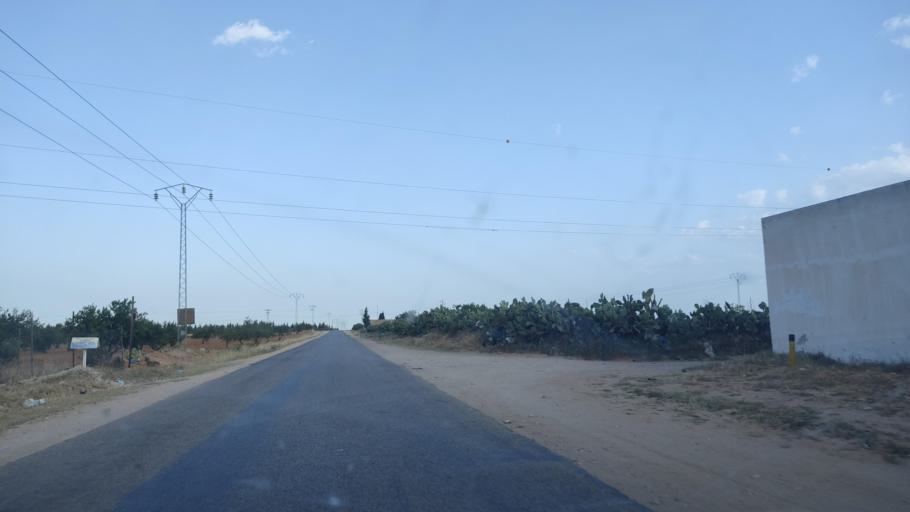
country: TN
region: Safaqis
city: Sfax
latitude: 34.8316
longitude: 10.6362
